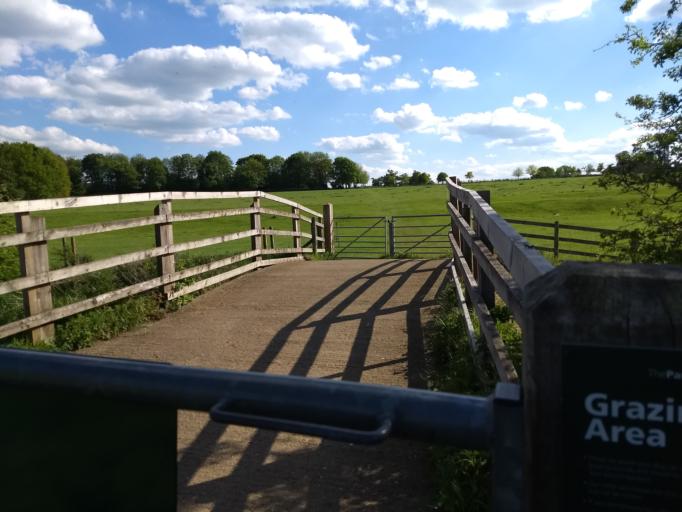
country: GB
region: England
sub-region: Milton Keynes
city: Castlethorpe
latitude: 52.0707
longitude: -0.8203
